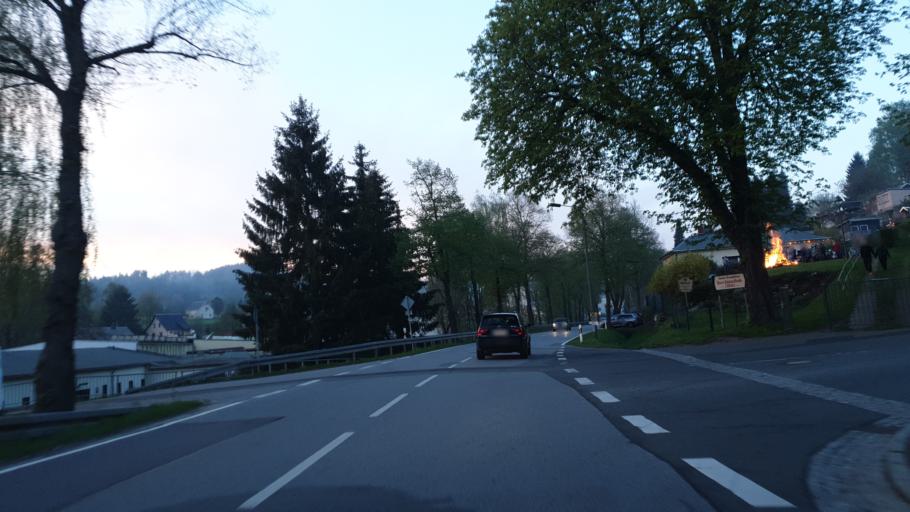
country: DE
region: Saxony
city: Lossnitz
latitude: 50.6263
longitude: 12.7360
